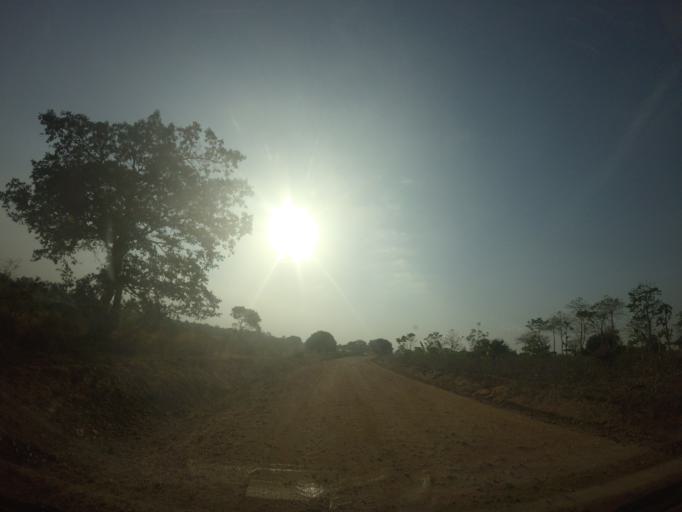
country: UG
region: Northern Region
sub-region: Arua District
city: Arua
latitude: 3.1001
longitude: 31.0889
